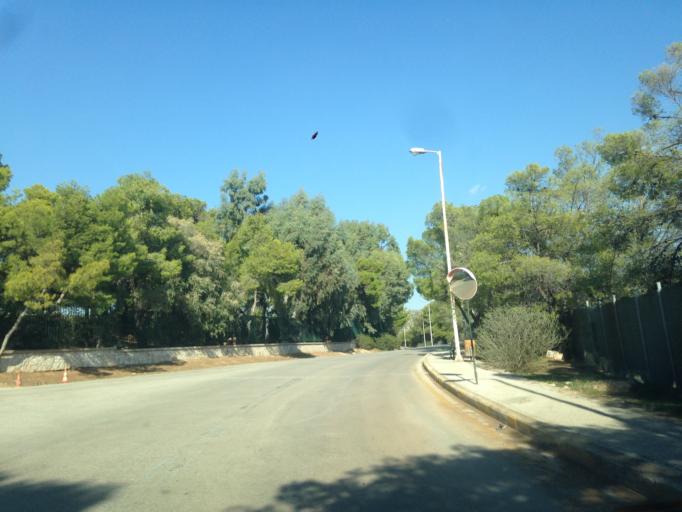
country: GR
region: Attica
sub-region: Nomarchia Anatolikis Attikis
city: Vouliagmeni
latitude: 37.8044
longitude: 23.7721
